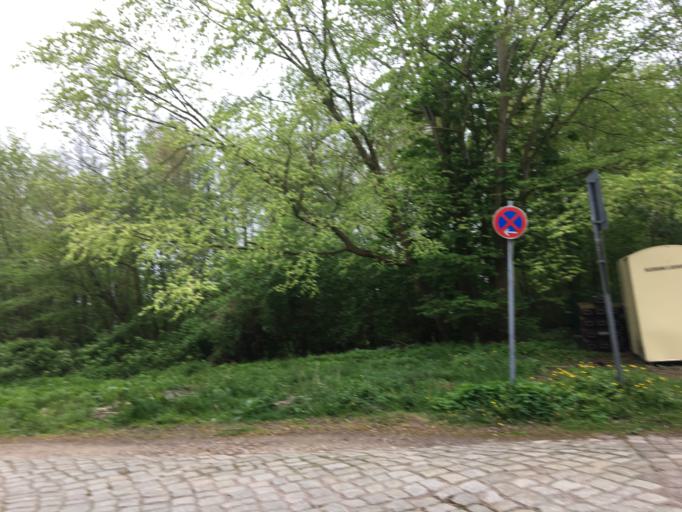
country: DE
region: Schleswig-Holstein
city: Tonning
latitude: 54.3139
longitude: 8.9388
